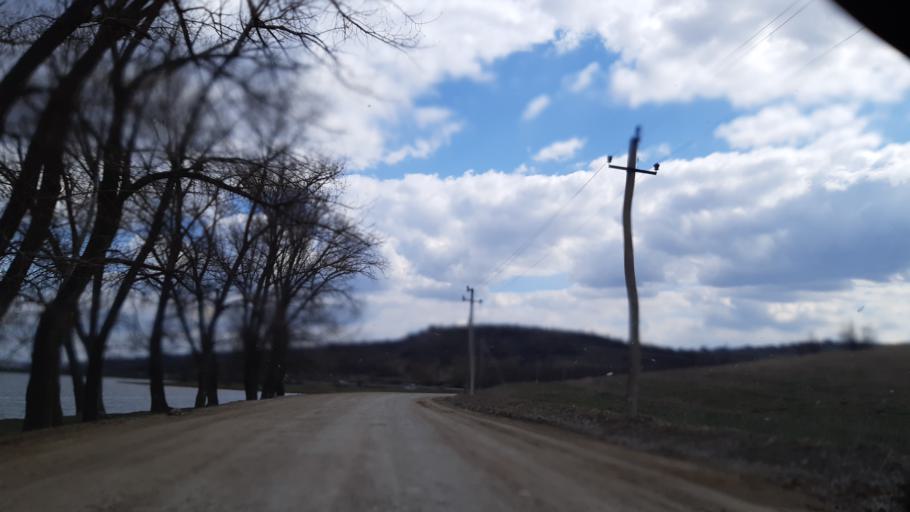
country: MD
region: Laloveni
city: Ialoveni
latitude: 46.8806
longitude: 28.7412
